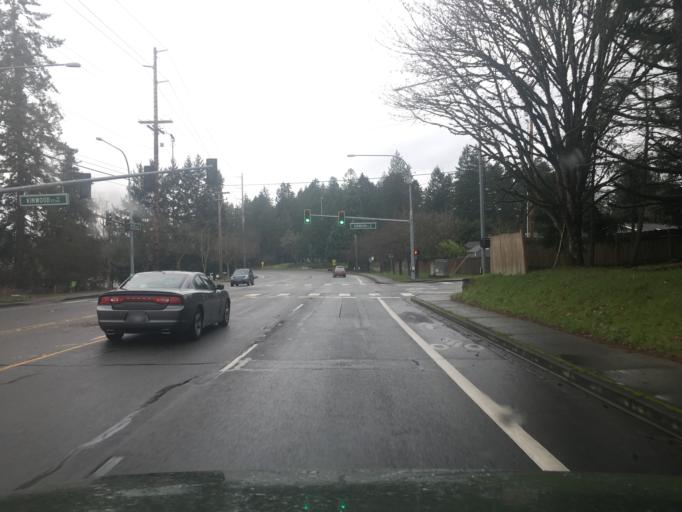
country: US
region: Washington
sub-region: Thurston County
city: Tanglewilde-Thompson Place
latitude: 47.0410
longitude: -122.7911
